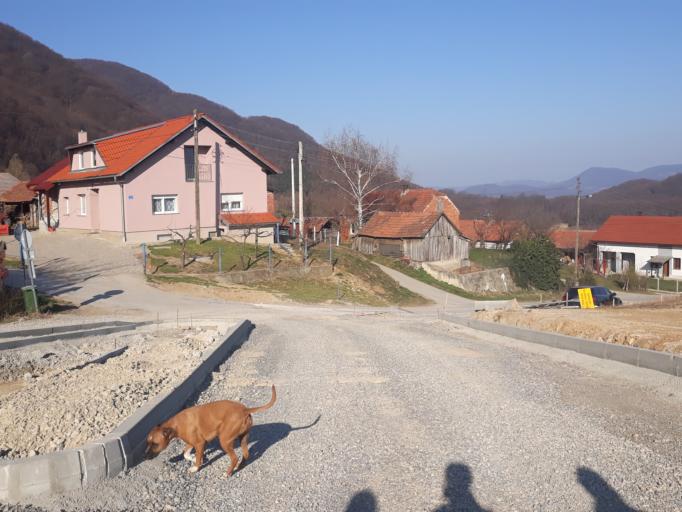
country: HR
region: Varazdinska
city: Ivanec
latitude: 46.1970
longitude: 16.1382
